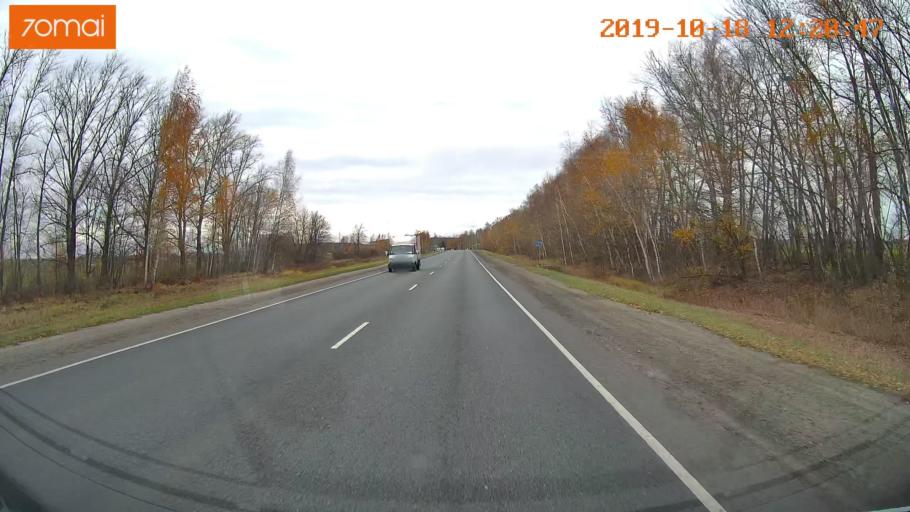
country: RU
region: Rjazan
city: Bagramovo
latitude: 54.5031
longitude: 39.4845
